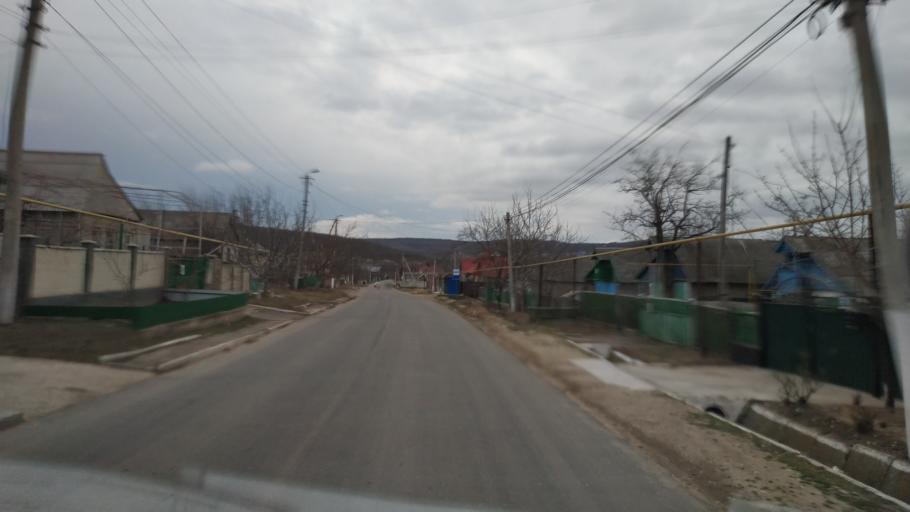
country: MD
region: Causeni
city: Causeni
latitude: 46.6557
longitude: 29.4444
